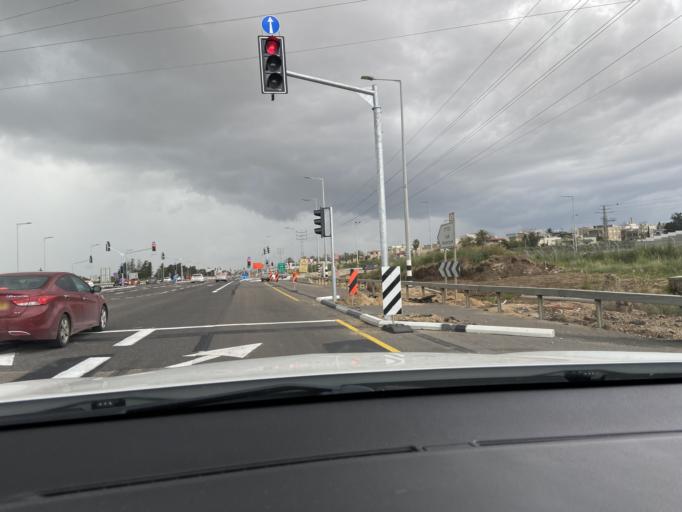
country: IL
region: Northern District
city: El Mazra`a
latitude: 32.9794
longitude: 35.0941
